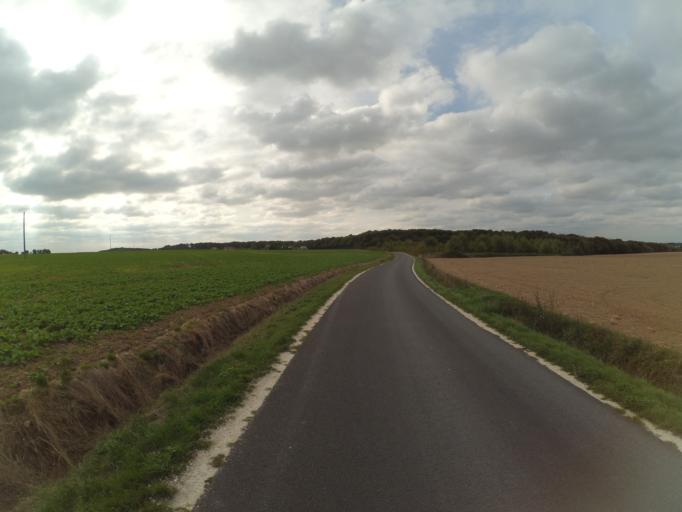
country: FR
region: Centre
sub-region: Departement d'Indre-et-Loire
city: Reugny
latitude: 47.4808
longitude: 0.9041
